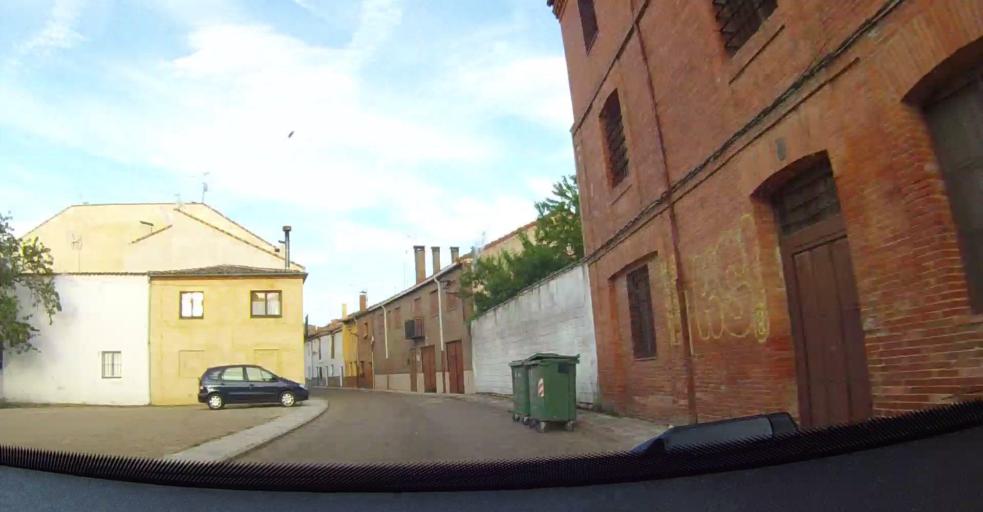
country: ES
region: Castille and Leon
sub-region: Provincia de Palencia
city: Carrion de los Condes
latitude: 42.3398
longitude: -4.6093
